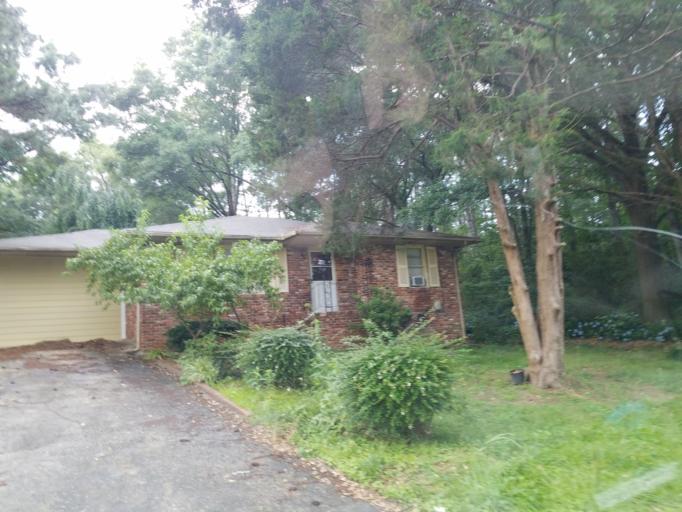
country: US
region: Georgia
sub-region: Cobb County
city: Marietta
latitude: 33.9691
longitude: -84.5305
